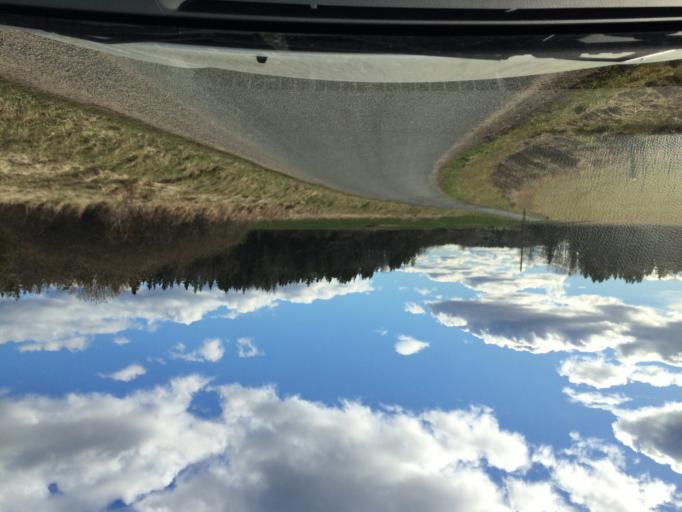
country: SE
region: Soedermanland
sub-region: Eskilstuna Kommun
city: Hallbybrunn
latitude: 59.4295
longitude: 16.4027
